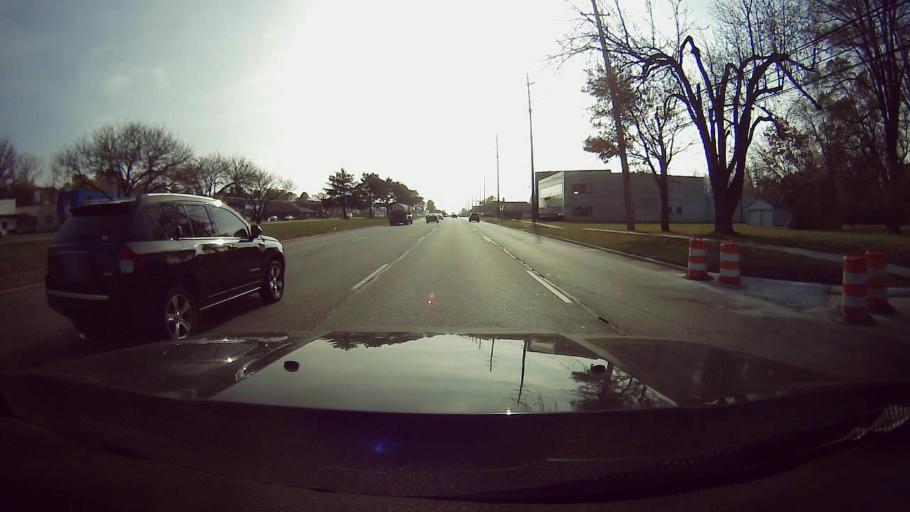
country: US
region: Michigan
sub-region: Oakland County
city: Bingham Farms
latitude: 42.4617
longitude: -83.2788
